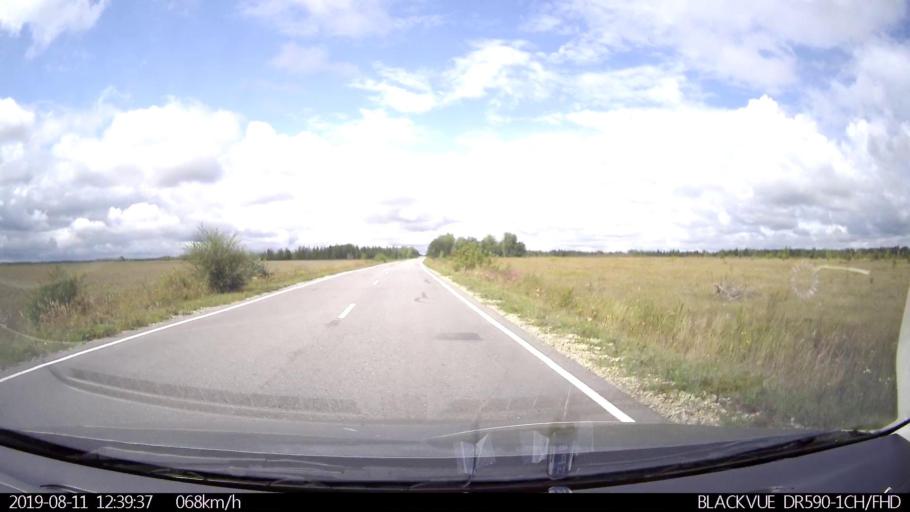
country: RU
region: Ulyanovsk
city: Ignatovka
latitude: 53.8342
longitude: 47.7927
